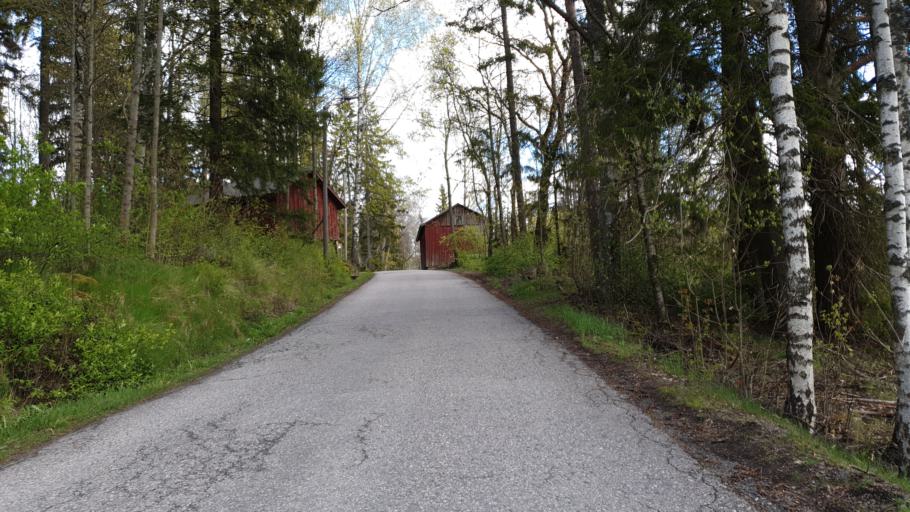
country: FI
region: Uusimaa
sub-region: Helsinki
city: Nurmijaervi
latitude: 60.3451
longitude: 24.8380
